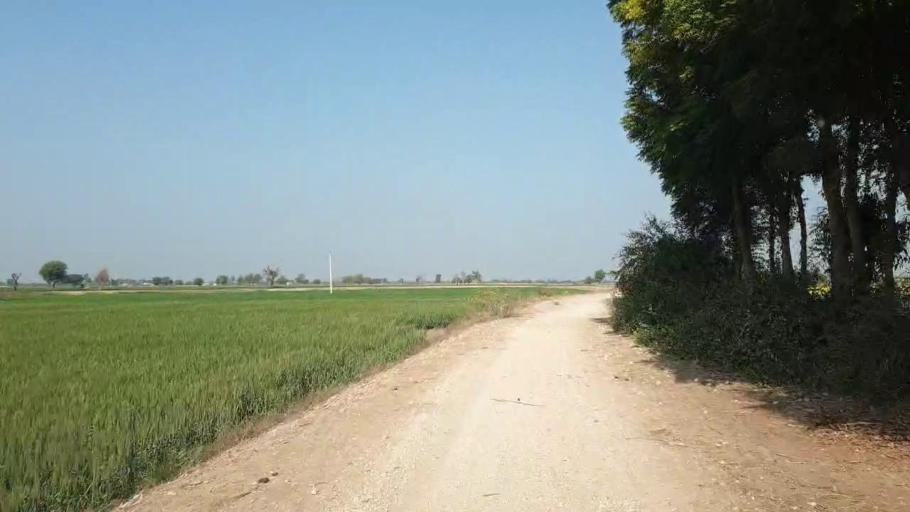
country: PK
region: Sindh
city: Hala
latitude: 25.9245
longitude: 68.4061
